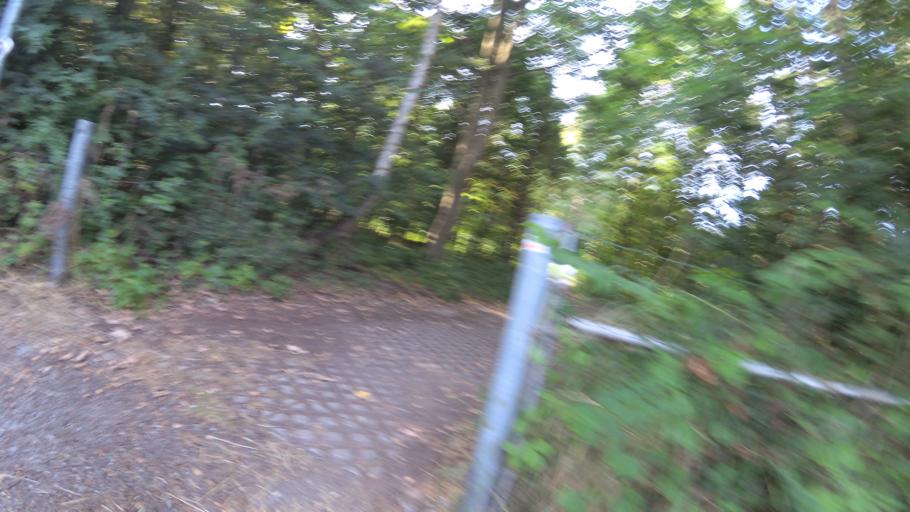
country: NL
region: Zeeland
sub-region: Gemeente Veere
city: Veere
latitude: 51.5735
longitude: 3.6606
